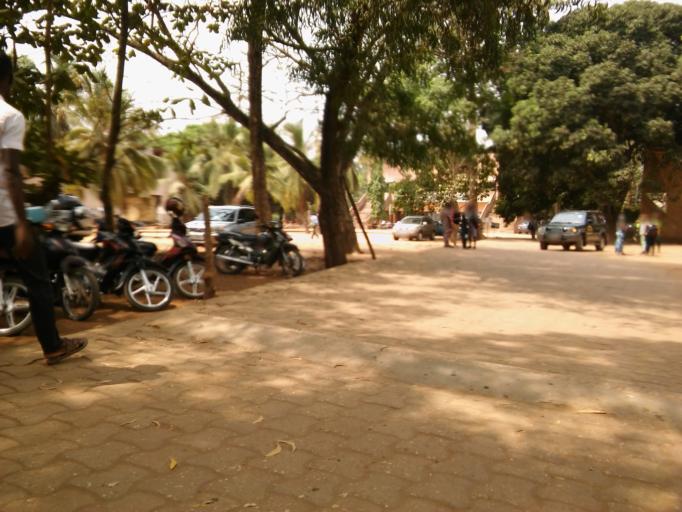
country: BJ
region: Atlantique
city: Abomey-Calavi
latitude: 6.4161
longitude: 2.3429
